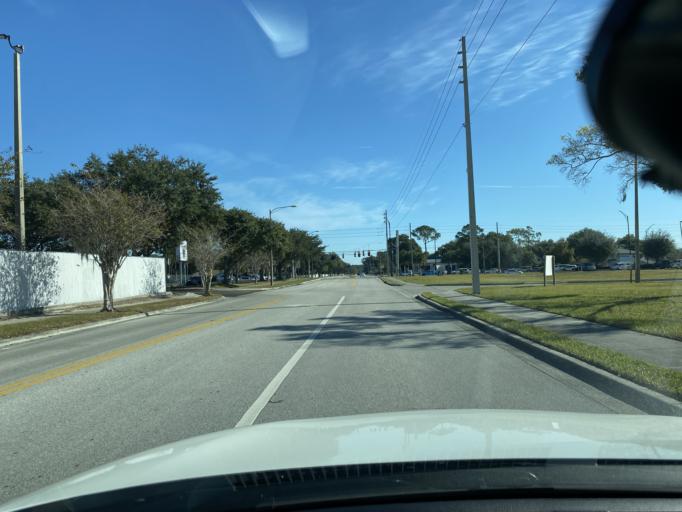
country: US
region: Florida
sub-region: Orange County
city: Conway
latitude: 28.5171
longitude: -81.3118
